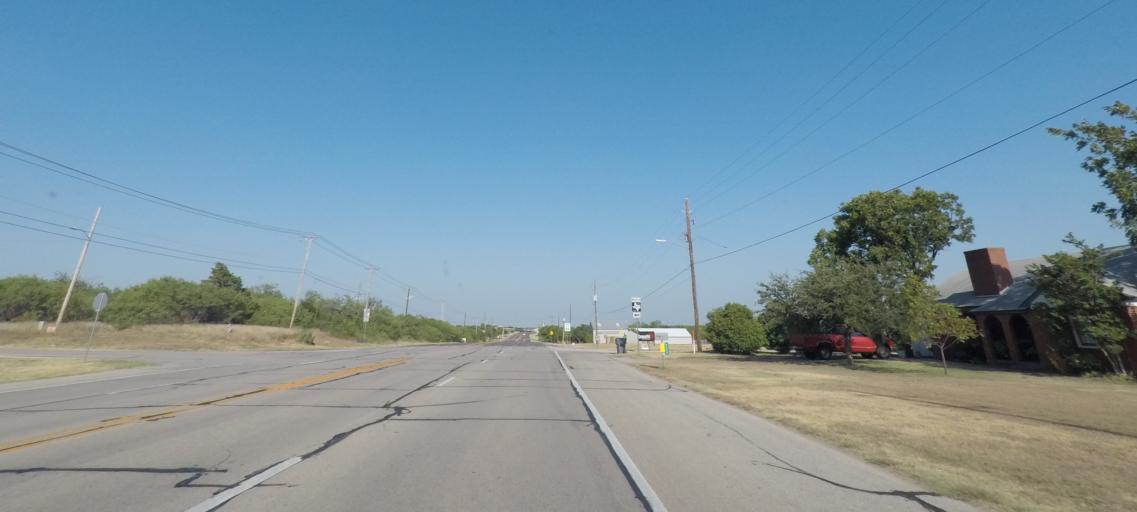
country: US
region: Texas
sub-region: Archer County
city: Holliday
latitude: 33.8593
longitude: -98.5967
